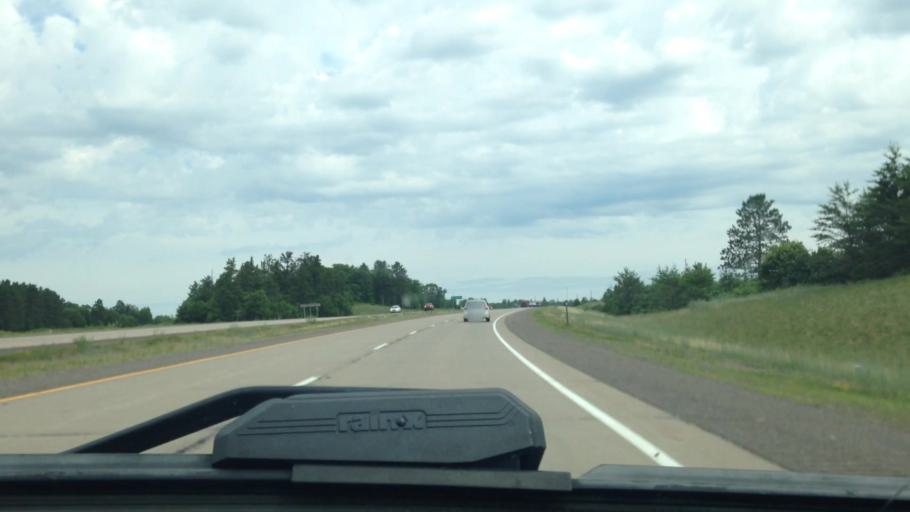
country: US
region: Wisconsin
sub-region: Douglas County
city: Lake Nebagamon
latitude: 46.2044
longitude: -91.7991
